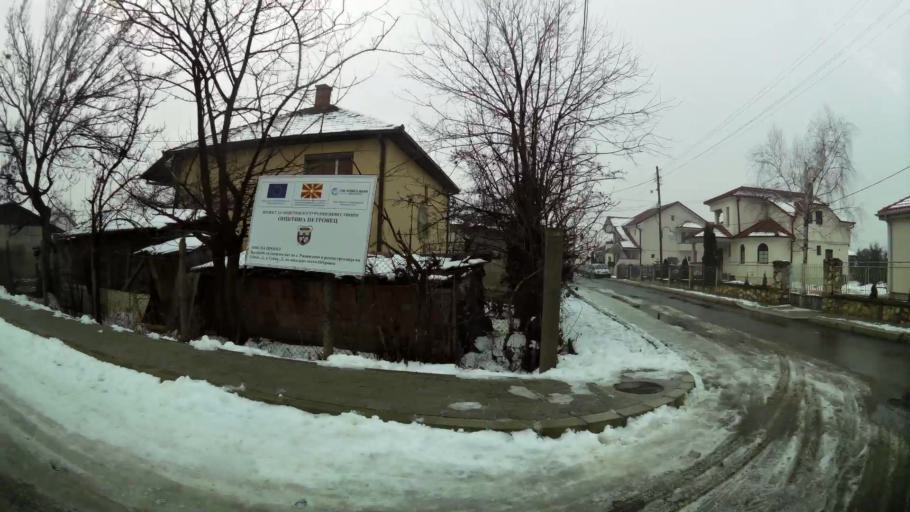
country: MK
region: Petrovec
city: Petrovec
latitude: 41.9424
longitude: 21.6113
